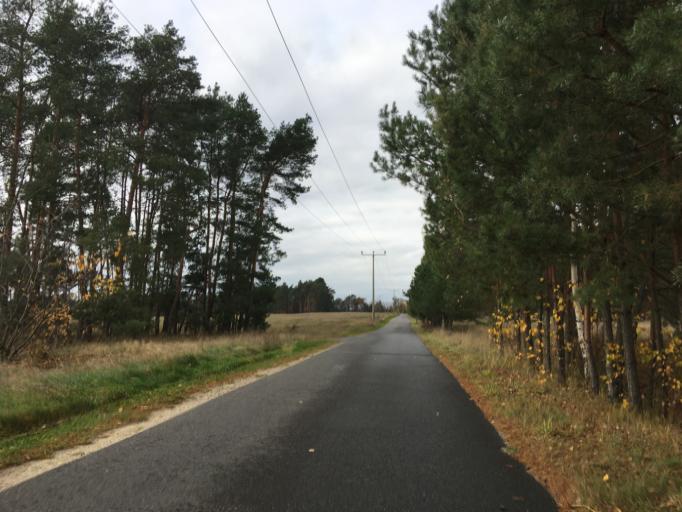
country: DE
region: Brandenburg
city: Jamlitz
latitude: 52.0839
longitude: 14.4440
